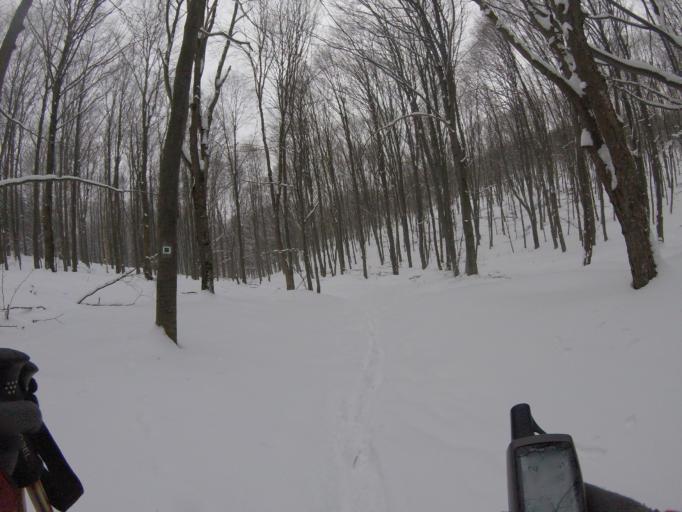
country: HU
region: Heves
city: Szilvasvarad
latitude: 48.0604
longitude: 20.4260
